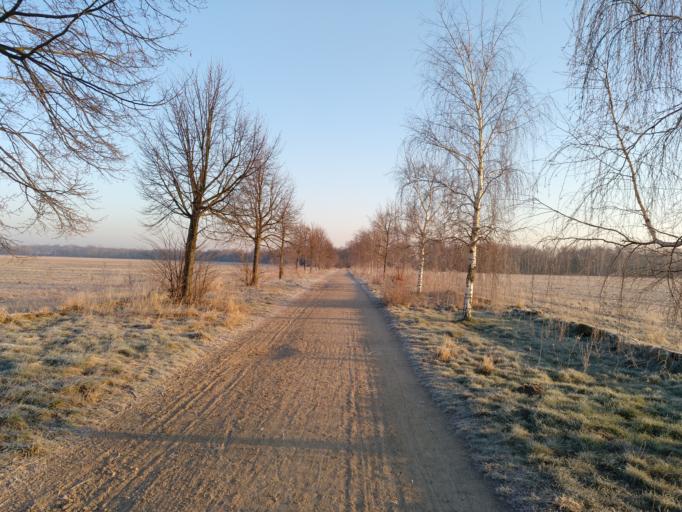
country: DE
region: Berlin
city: Marienfelde
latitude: 52.3858
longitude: 13.3674
